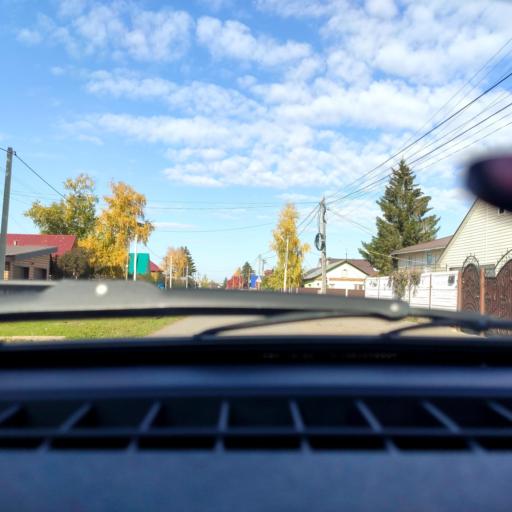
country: RU
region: Bashkortostan
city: Ufa
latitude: 54.6120
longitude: 55.9434
